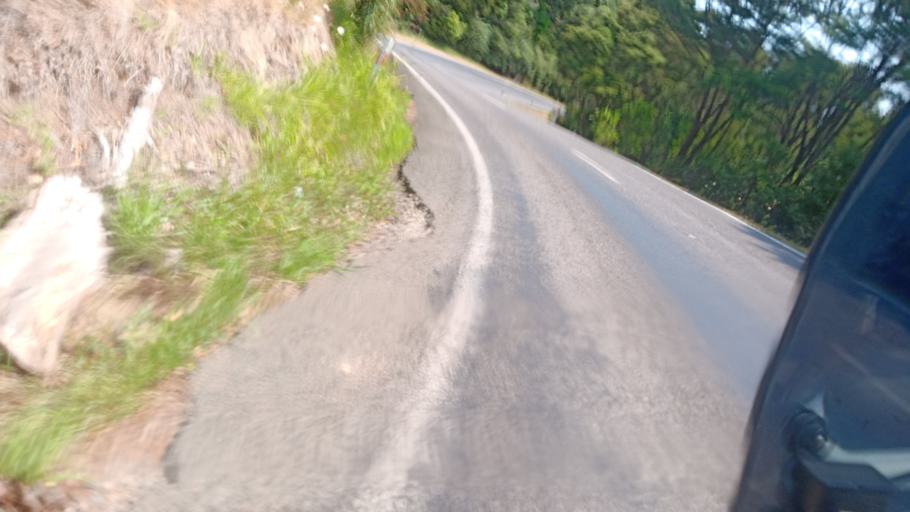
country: NZ
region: Bay of Plenty
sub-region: Opotiki District
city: Opotiki
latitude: -37.5744
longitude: 178.0779
